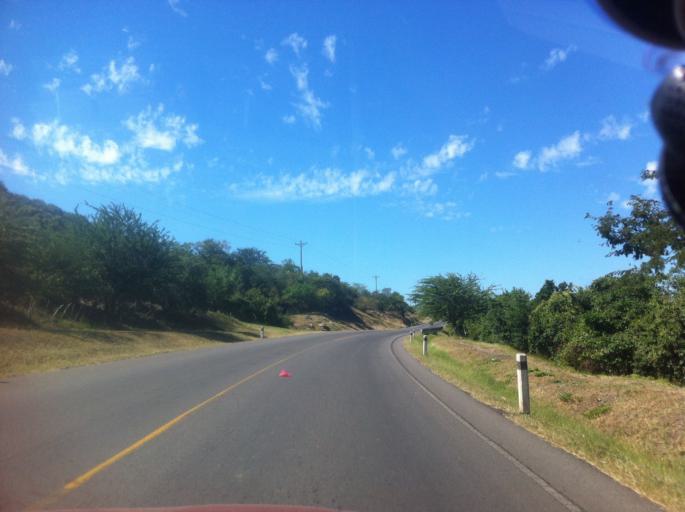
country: NI
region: Boaco
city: Teustepe
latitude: 12.4144
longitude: -85.8237
